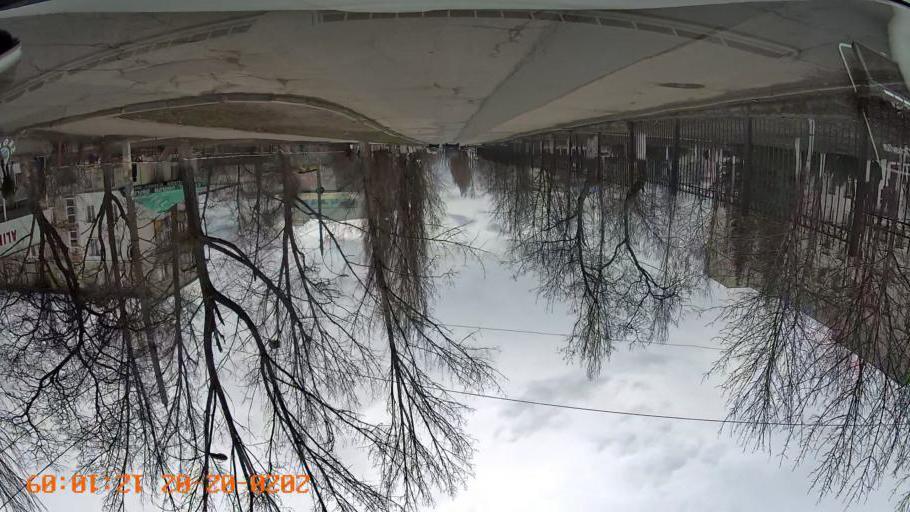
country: MD
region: Chisinau
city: Chisinau
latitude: 46.9989
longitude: 28.8050
